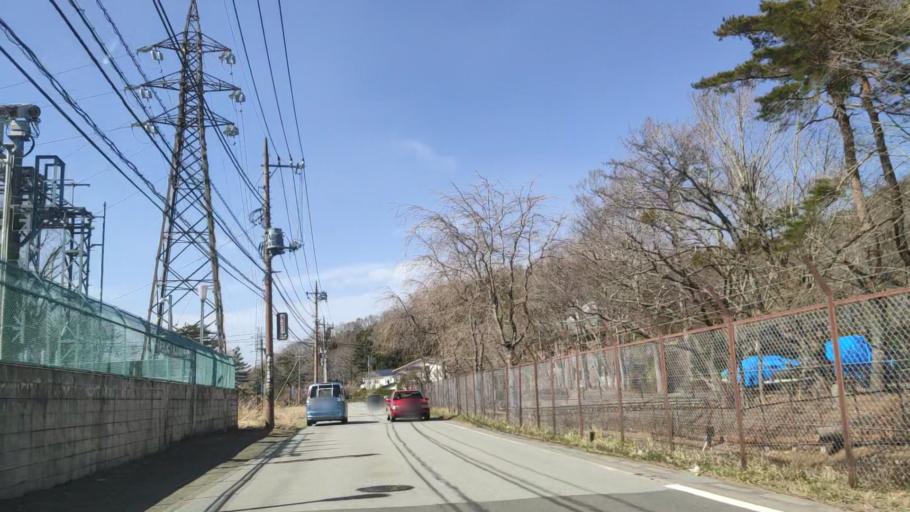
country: JP
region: Shizuoka
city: Gotemba
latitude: 35.4295
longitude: 138.8517
